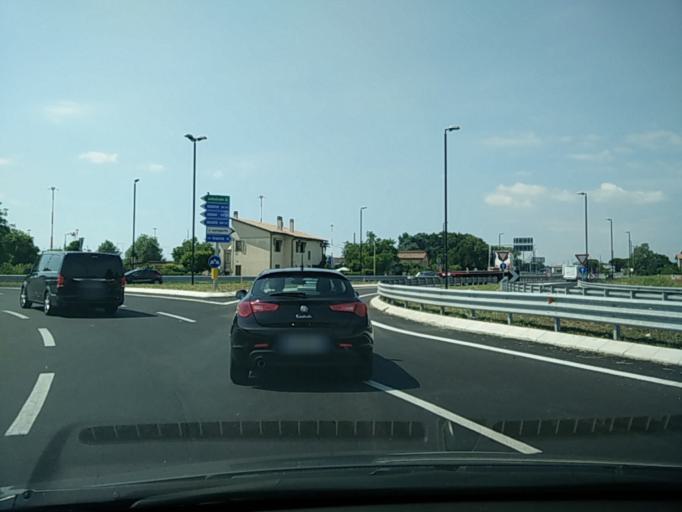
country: IT
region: Veneto
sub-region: Provincia di Venezia
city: Tessera
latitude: 45.5115
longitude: 12.3395
